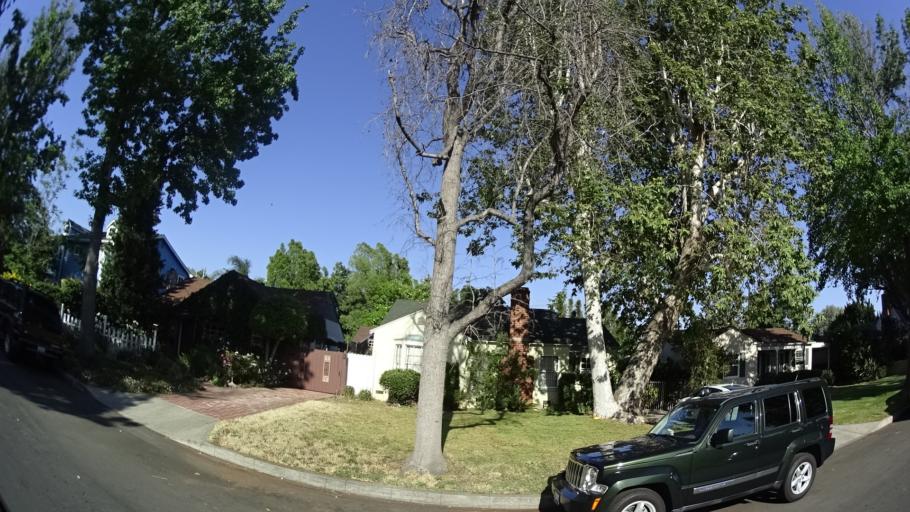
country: US
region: California
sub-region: Los Angeles County
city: North Hollywood
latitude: 34.1602
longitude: -118.3627
